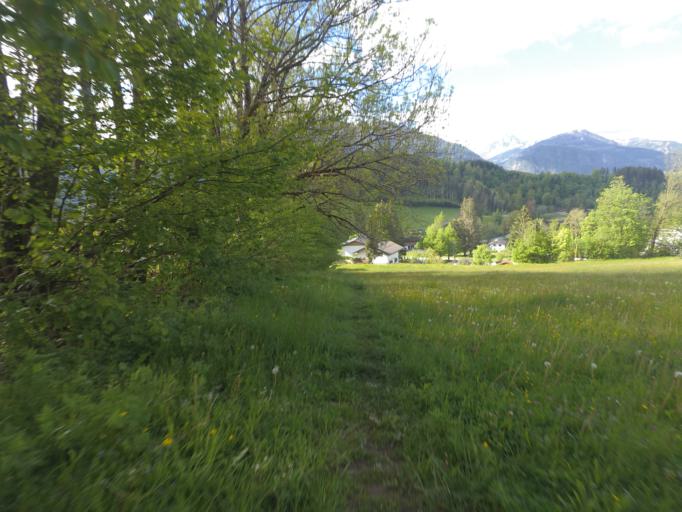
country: AT
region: Salzburg
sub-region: Politischer Bezirk Sankt Johann im Pongau
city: Goldegg
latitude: 47.3196
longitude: 13.1081
